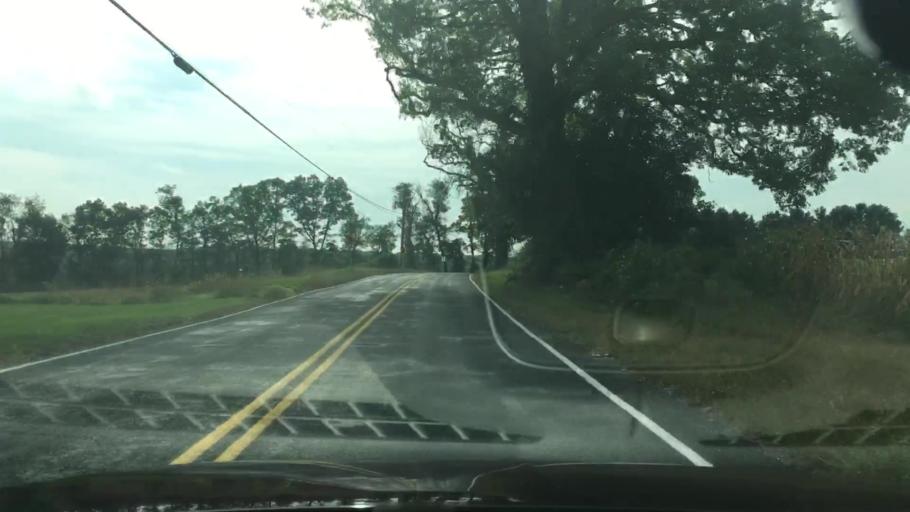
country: US
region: Connecticut
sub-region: Tolland County
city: Somers
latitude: 41.9670
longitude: -72.4824
